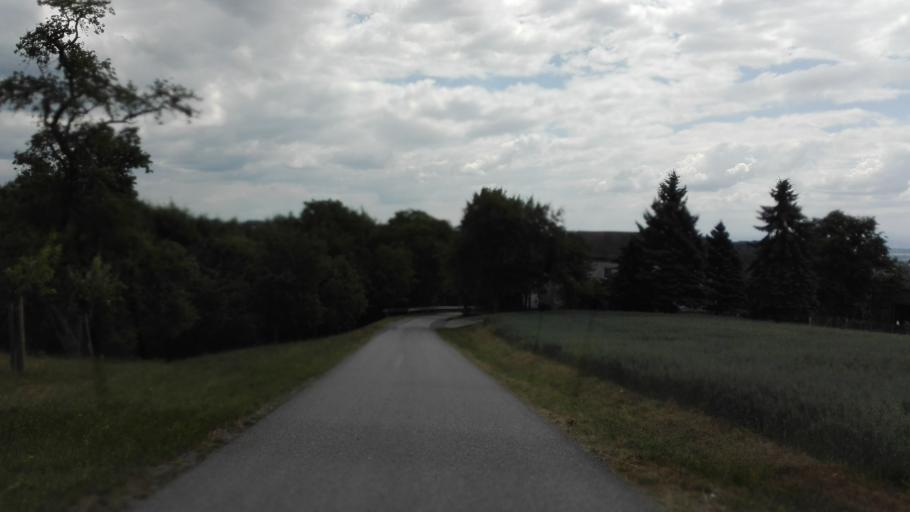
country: AT
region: Upper Austria
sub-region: Politischer Bezirk Perg
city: Bad Kreuzen
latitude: 48.2442
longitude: 14.7336
